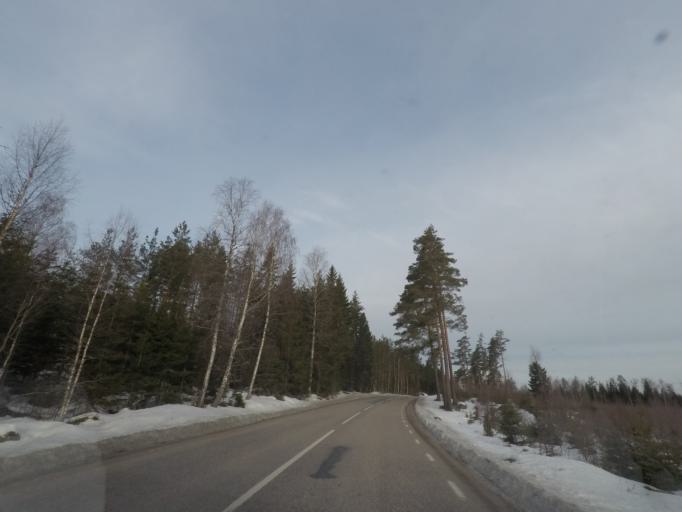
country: SE
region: Vaestmanland
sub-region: Surahammars Kommun
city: Surahammar
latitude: 59.7581
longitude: 16.3028
